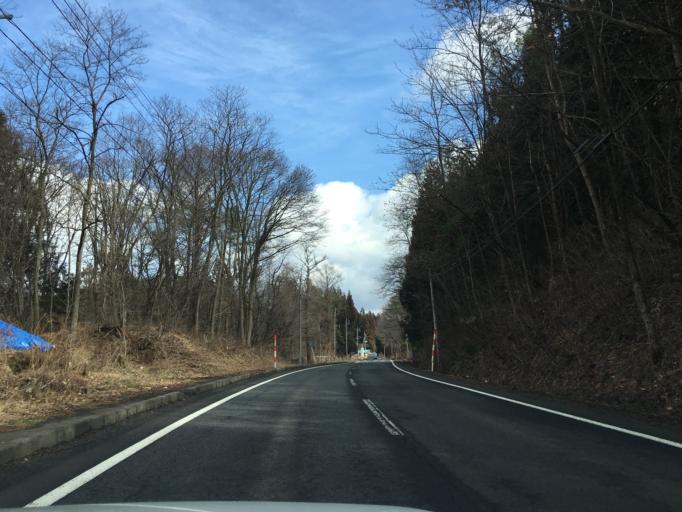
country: JP
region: Akita
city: Odate
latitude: 40.2015
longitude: 140.5504
